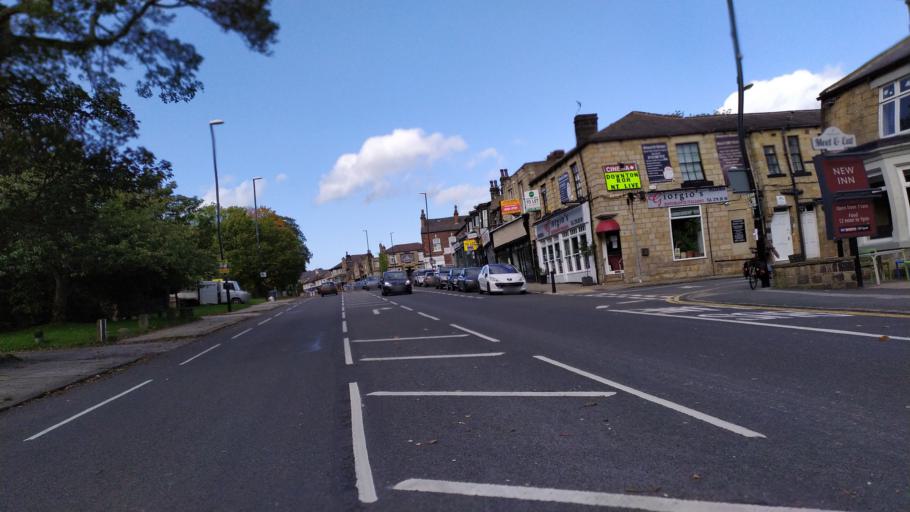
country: GB
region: England
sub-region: City and Borough of Leeds
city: Chapel Allerton
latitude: 53.8265
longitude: -1.5820
